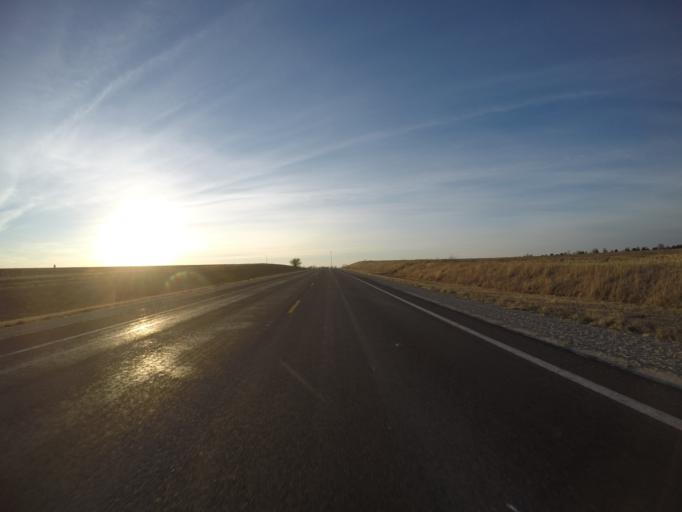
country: US
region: Kansas
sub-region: Riley County
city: Fort Riley North
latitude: 39.3009
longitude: -96.8139
